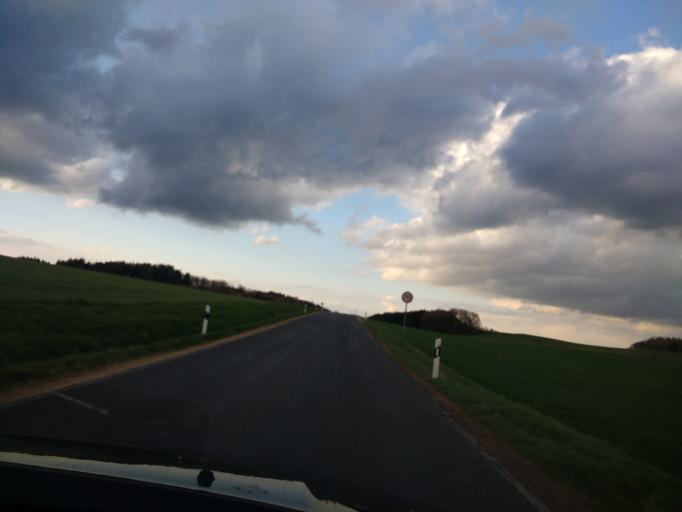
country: DE
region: Rheinland-Pfalz
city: Basberg
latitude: 50.2789
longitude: 6.6090
